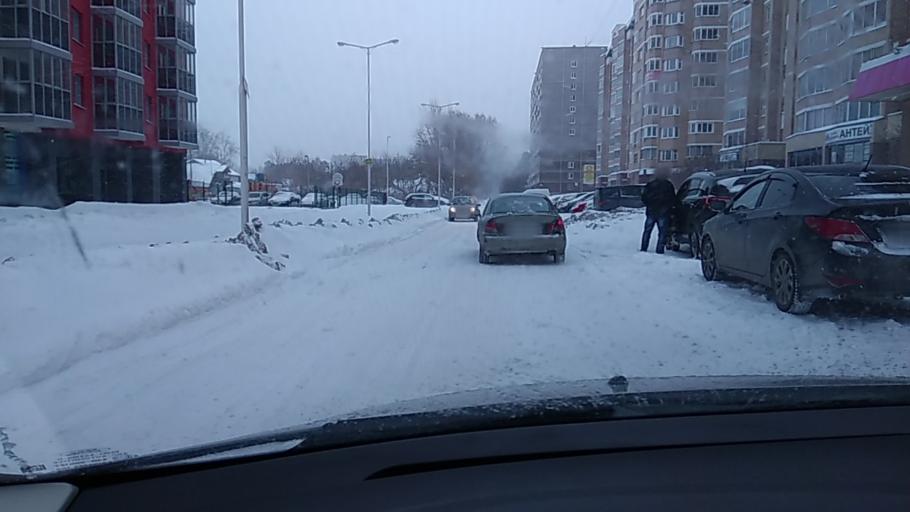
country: RU
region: Sverdlovsk
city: Sovkhoznyy
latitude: 56.8208
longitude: 60.5449
